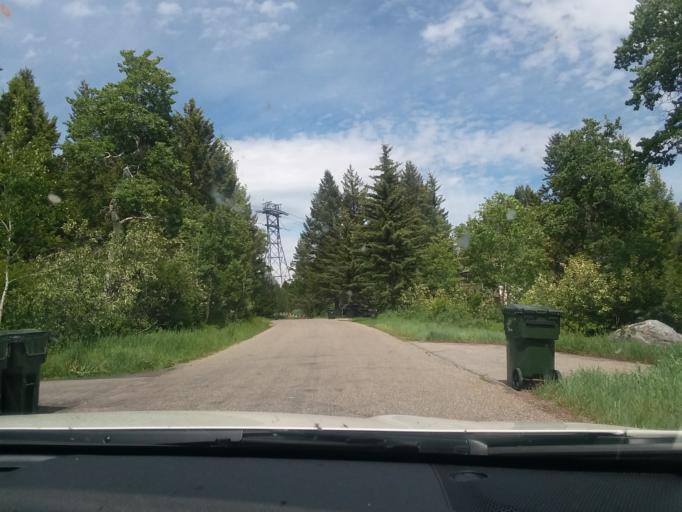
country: US
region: Wyoming
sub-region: Teton County
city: Moose Wilson Road
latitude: 43.5864
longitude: -110.8343
